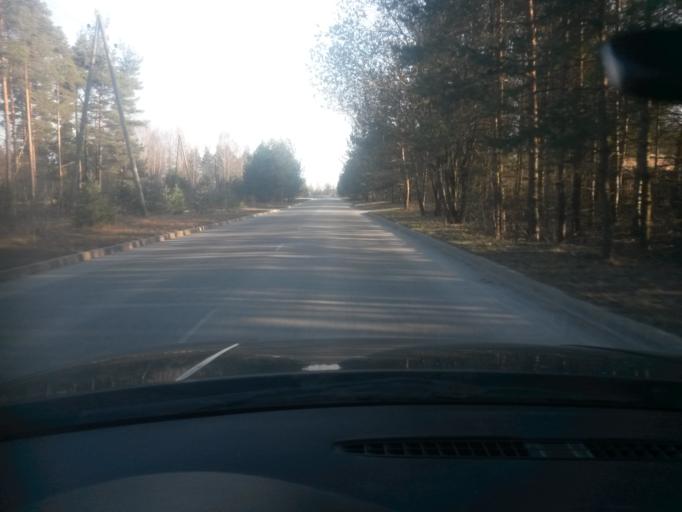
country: LV
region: Stopini
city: Ulbroka
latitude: 56.8995
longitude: 24.2472
